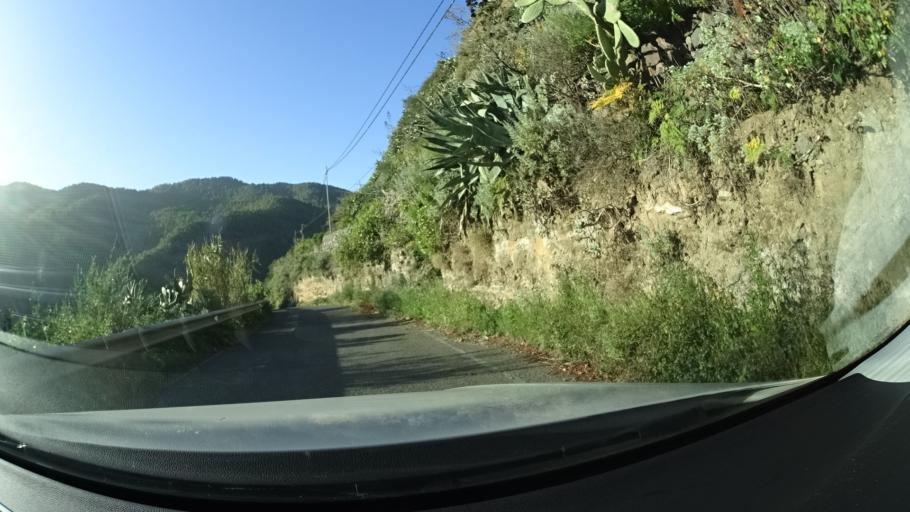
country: ES
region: Canary Islands
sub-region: Provincia de Las Palmas
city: Artenara
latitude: 28.0472
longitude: -15.6653
